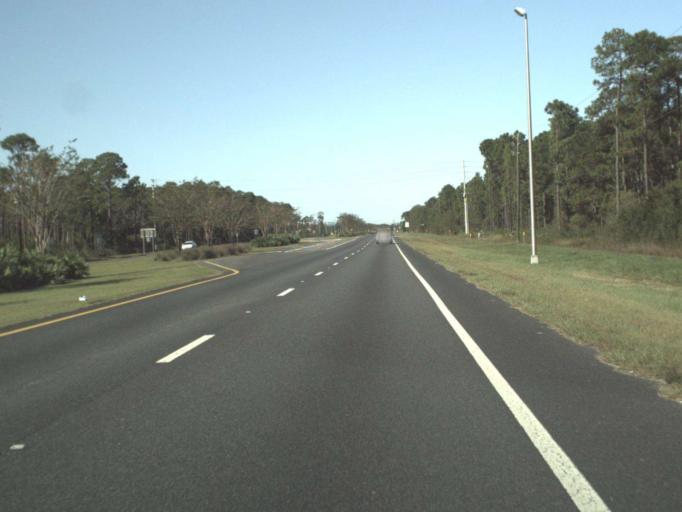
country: US
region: Florida
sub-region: Walton County
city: Miramar Beach
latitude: 30.3755
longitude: -86.2773
